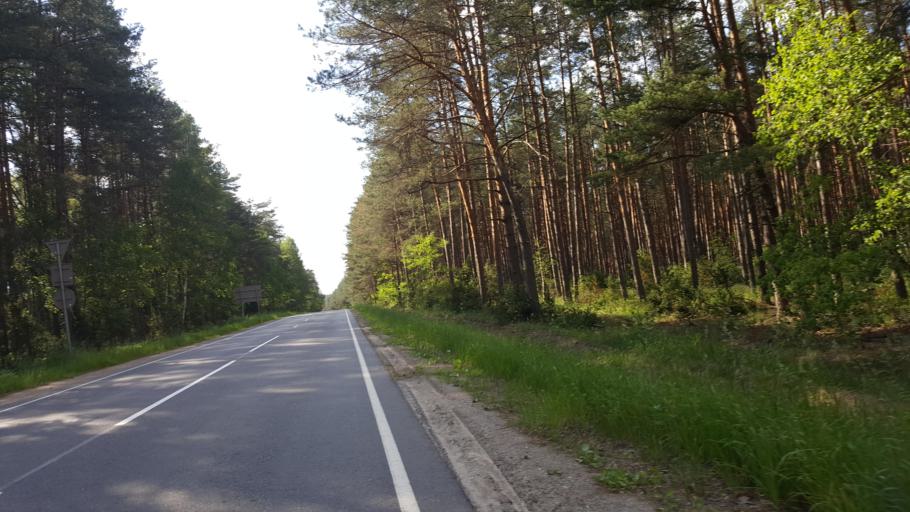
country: BY
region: Brest
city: Zhabinka
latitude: 52.3810
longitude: 24.1199
